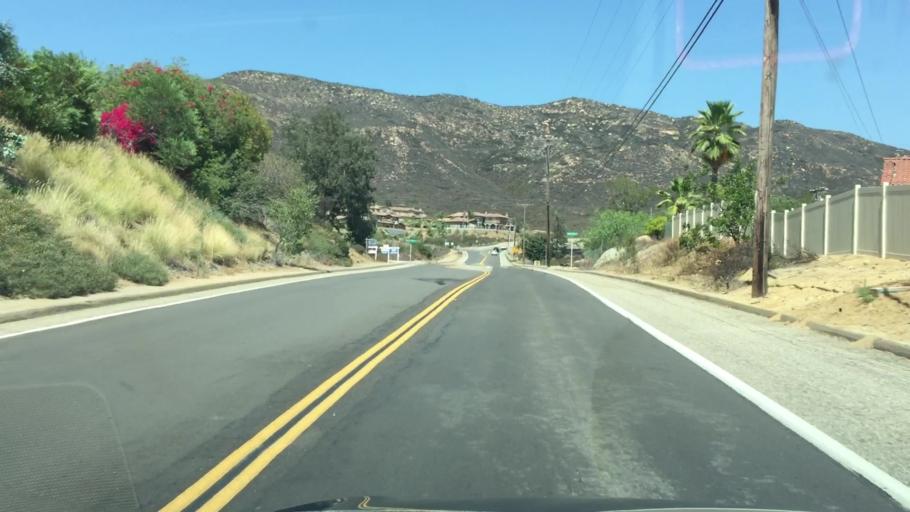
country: US
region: California
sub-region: San Diego County
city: Jamul
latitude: 32.7328
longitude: -116.8529
